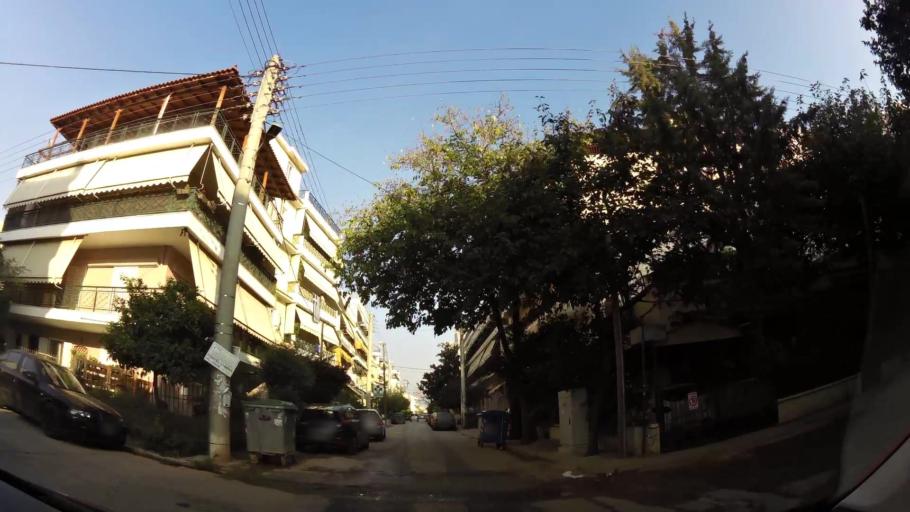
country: GR
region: Attica
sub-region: Nomarchia Anatolikis Attikis
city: Acharnes
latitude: 38.0853
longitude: 23.7430
